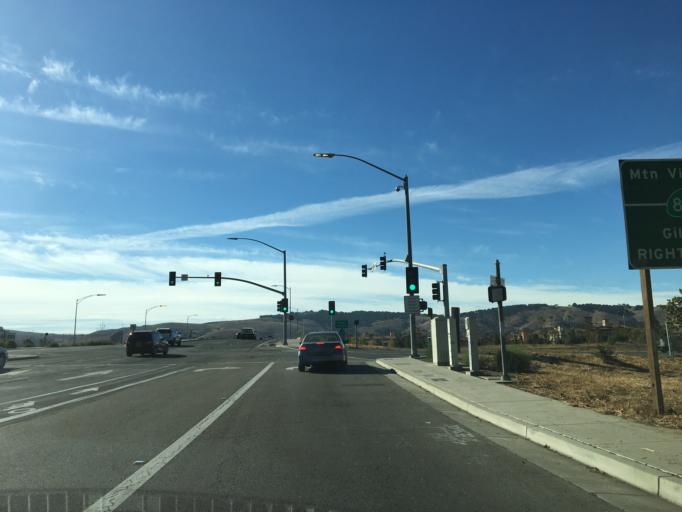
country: US
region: California
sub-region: Santa Clara County
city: Seven Trees
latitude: 37.2449
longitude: -121.8042
